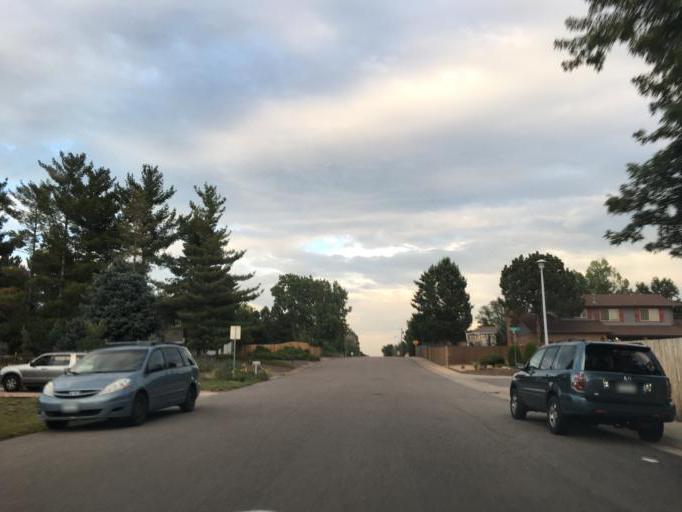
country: US
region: Colorado
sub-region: Adams County
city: Aurora
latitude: 39.6802
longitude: -104.8636
